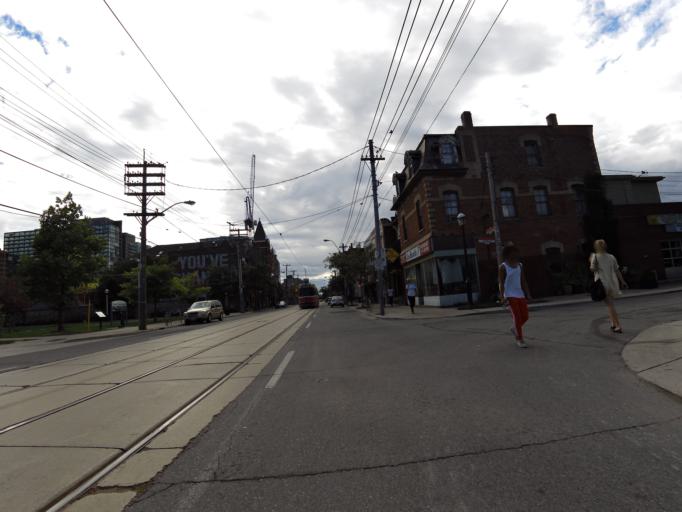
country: CA
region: Ontario
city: Toronto
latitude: 43.6438
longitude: -79.4211
